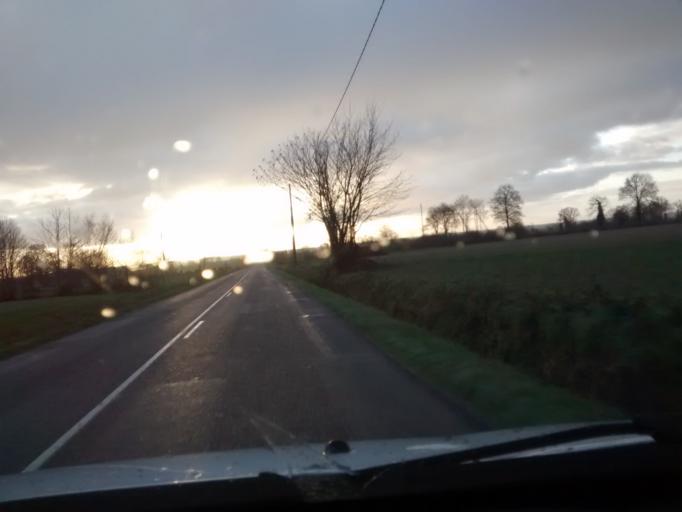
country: FR
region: Brittany
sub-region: Departement d'Ille-et-Vilaine
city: Bais
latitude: 47.9851
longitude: -1.2836
